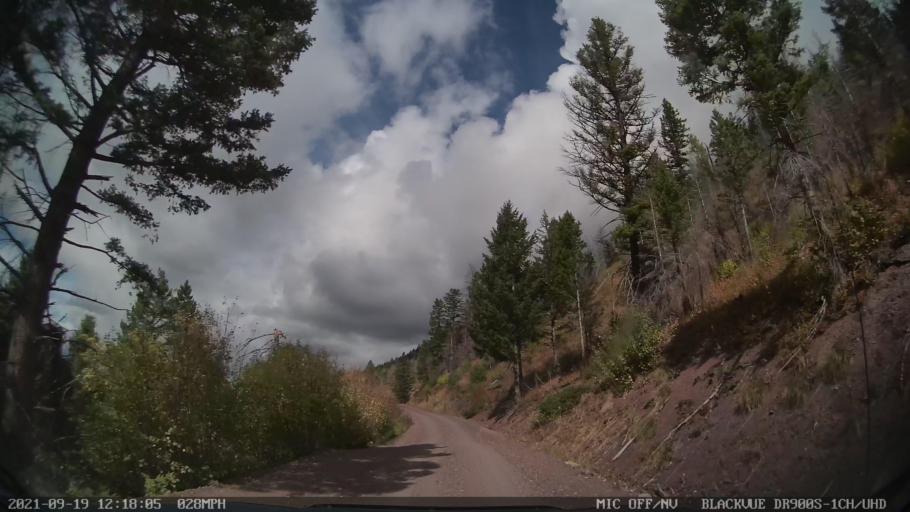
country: US
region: Montana
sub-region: Missoula County
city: Seeley Lake
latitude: 47.1743
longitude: -113.3630
